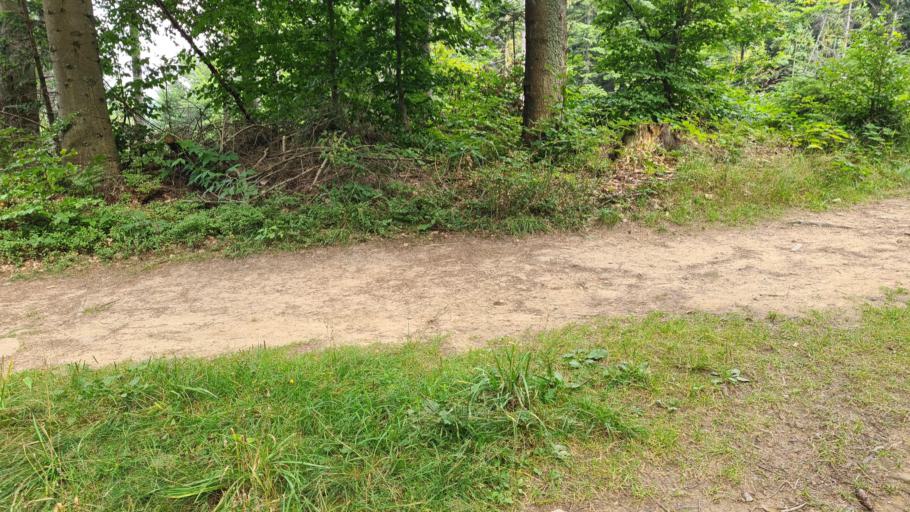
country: PL
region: Lesser Poland Voivodeship
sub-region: Powiat nowosadecki
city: Rytro
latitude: 49.4122
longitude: 20.6235
